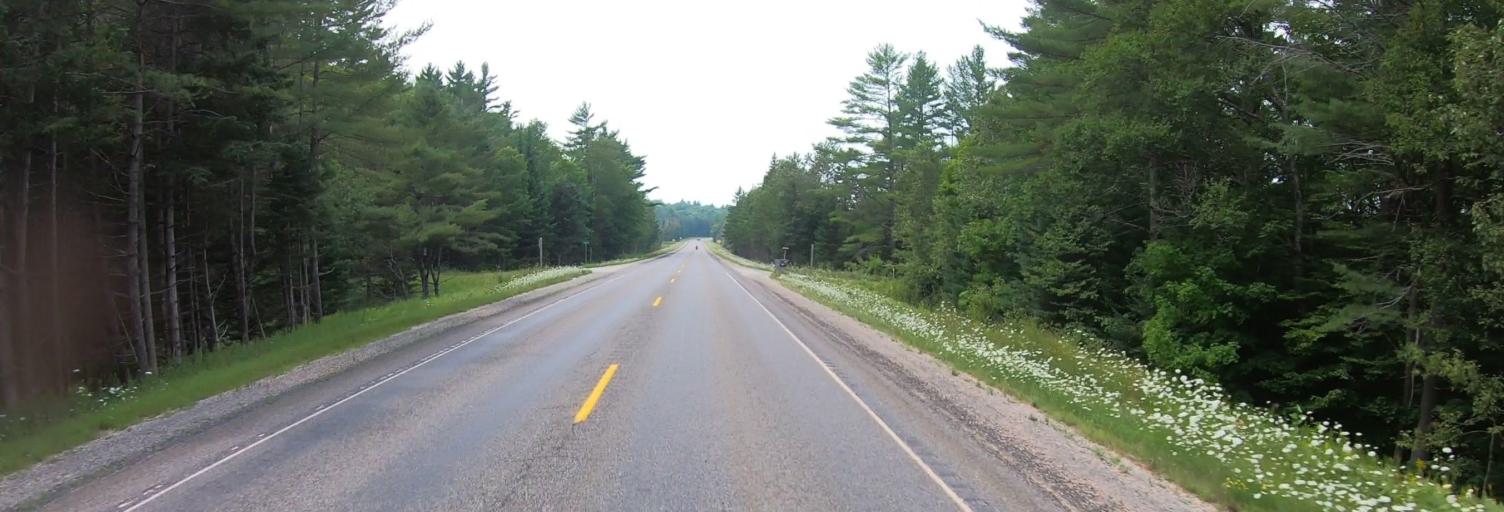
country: US
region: Michigan
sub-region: Alger County
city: Munising
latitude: 46.3329
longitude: -86.8188
